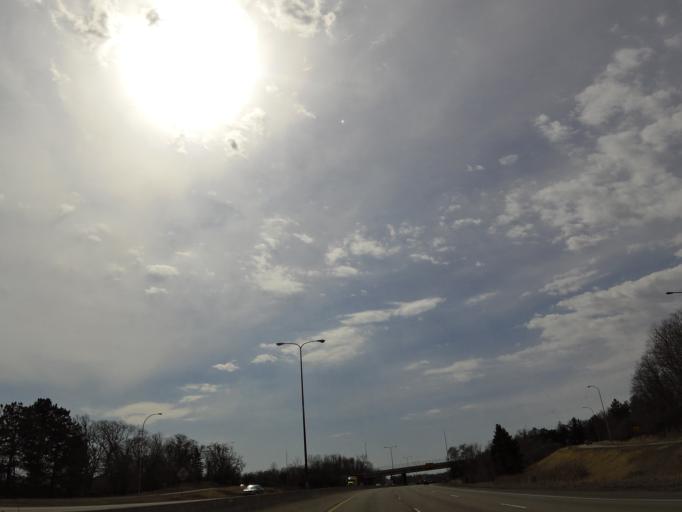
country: US
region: Minnesota
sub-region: Dakota County
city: South Saint Paul
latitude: 44.9148
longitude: -93.0636
